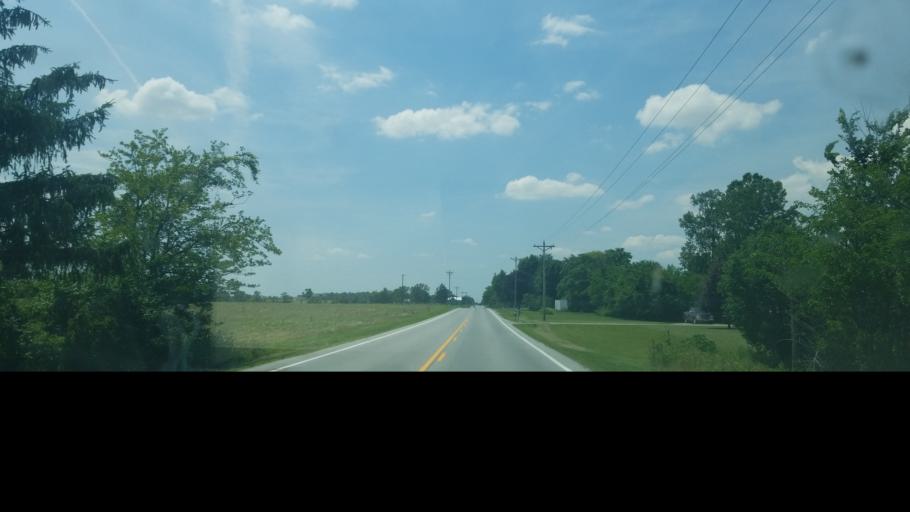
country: US
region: Ohio
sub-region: Hardin County
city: Ada
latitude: 40.7760
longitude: -83.8961
